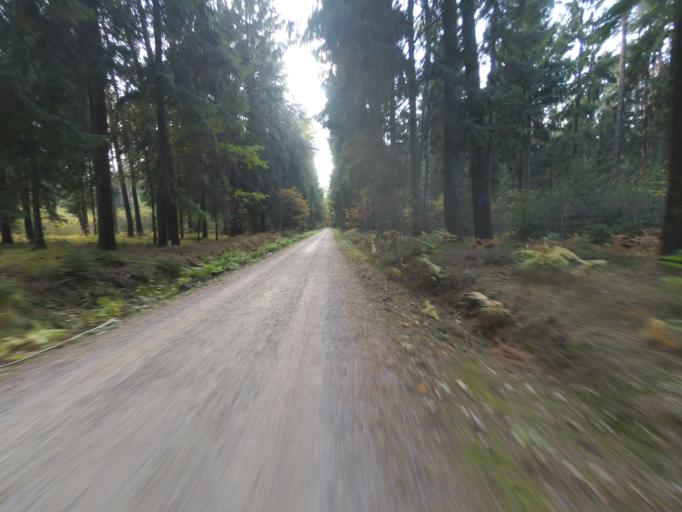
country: DE
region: Saxony
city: Radeberg
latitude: 51.0751
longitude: 13.8491
